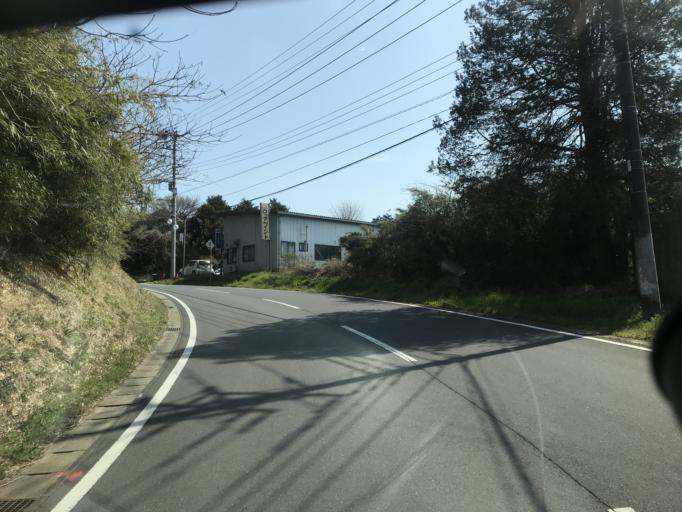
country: JP
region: Chiba
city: Omigawa
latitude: 35.8532
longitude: 140.5554
